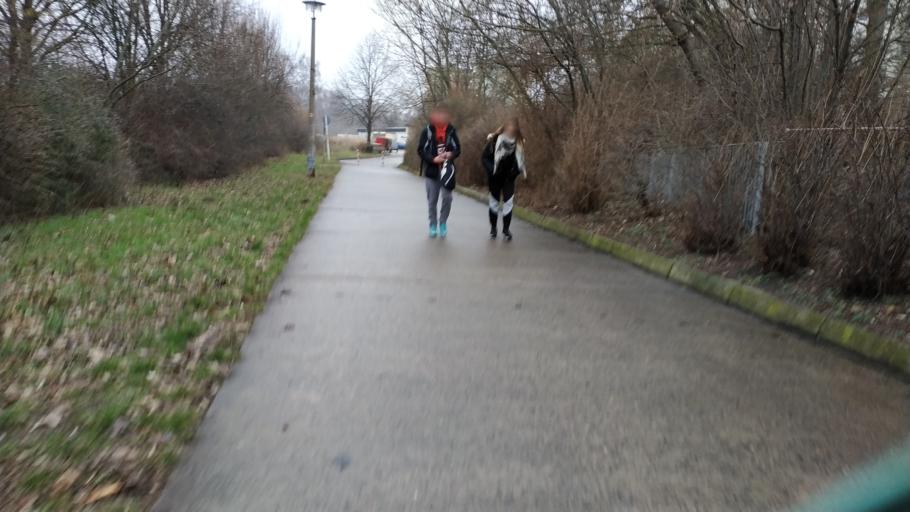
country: DE
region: Berlin
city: Marzahn
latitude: 52.5432
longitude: 13.5843
